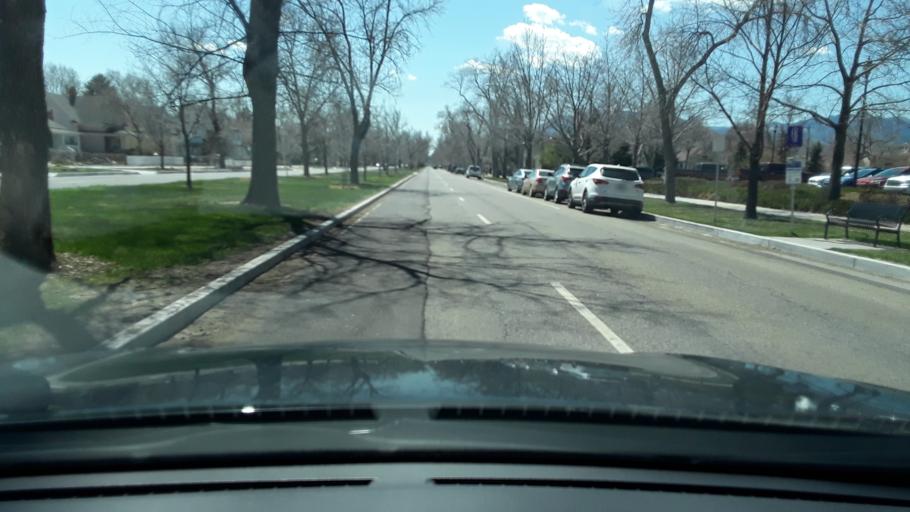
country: US
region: Colorado
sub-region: El Paso County
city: Colorado Springs
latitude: 38.8655
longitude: -104.8202
